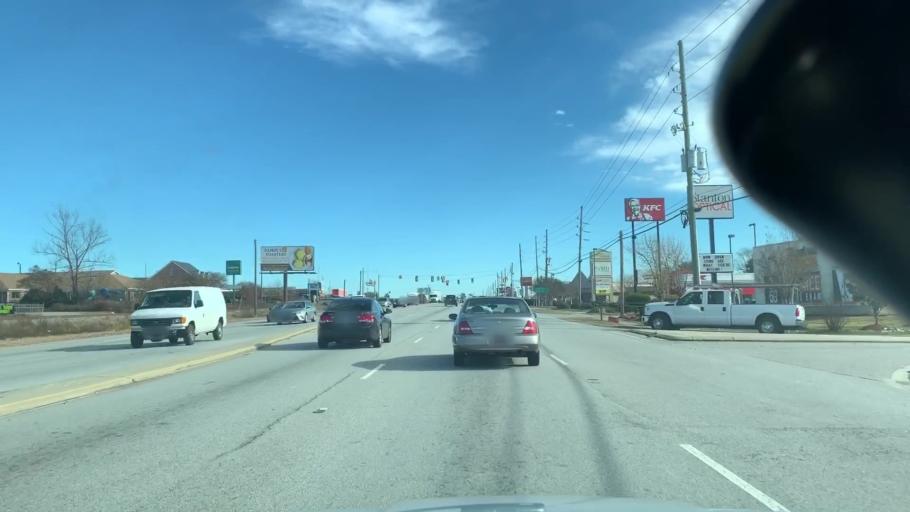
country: US
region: South Carolina
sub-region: Richland County
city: Woodfield
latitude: 34.1154
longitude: -80.8870
